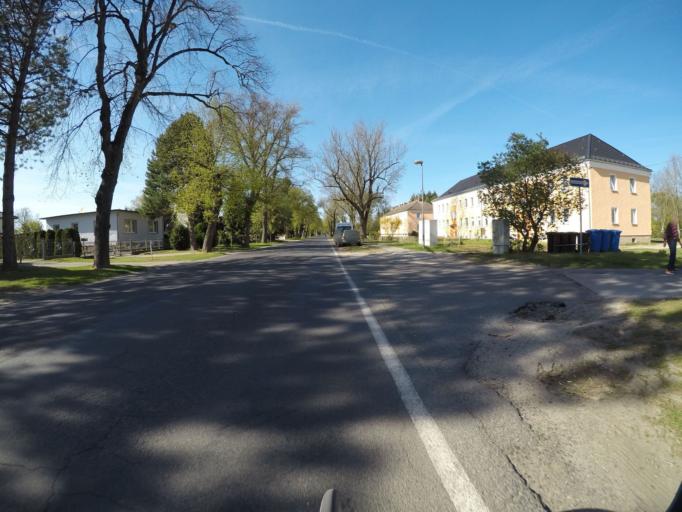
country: DE
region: Brandenburg
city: Rehfelde
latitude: 52.4755
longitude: 13.8535
